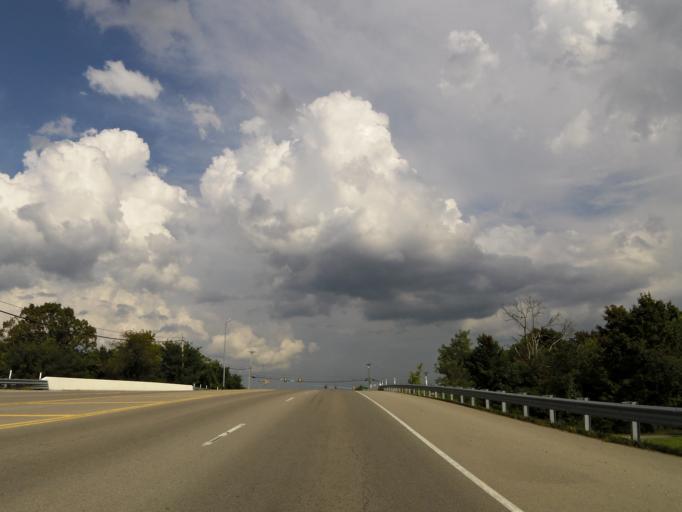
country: US
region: Tennessee
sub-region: Dickson County
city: Dickson
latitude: 36.0858
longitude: -87.4017
